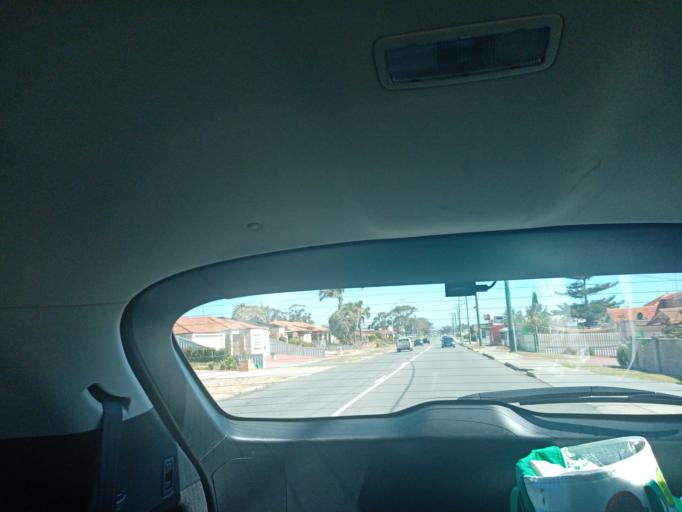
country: AU
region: Western Australia
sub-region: City of Cockburn
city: Spearwood
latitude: -32.1121
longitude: 115.7827
